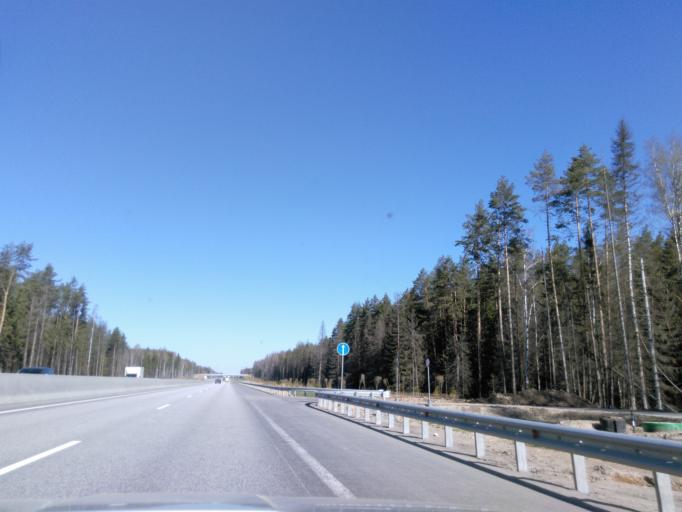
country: RU
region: Moskovskaya
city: Mendeleyevo
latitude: 56.0568
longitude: 37.2492
